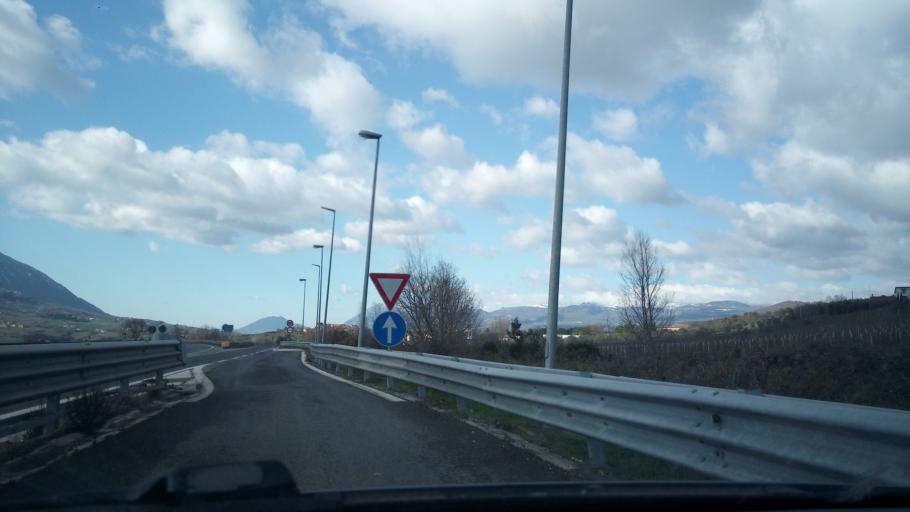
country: IT
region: Campania
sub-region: Provincia di Benevento
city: Ponte
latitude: 41.1876
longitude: 14.7451
